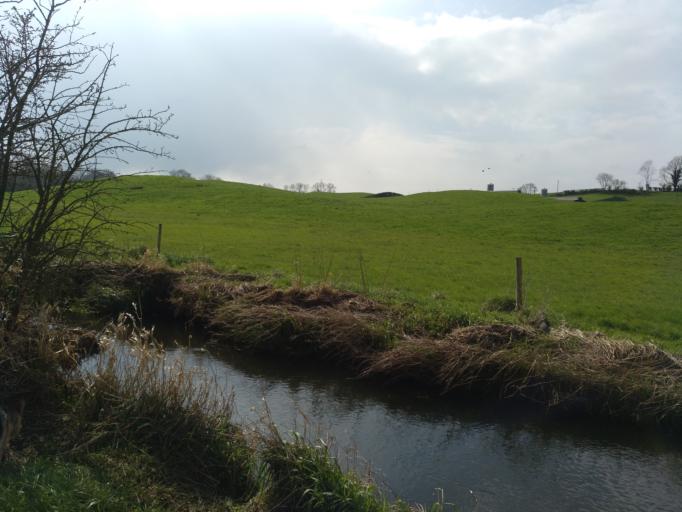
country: IE
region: Ulster
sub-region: County Monaghan
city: Clones
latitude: 54.2113
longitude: -7.1187
